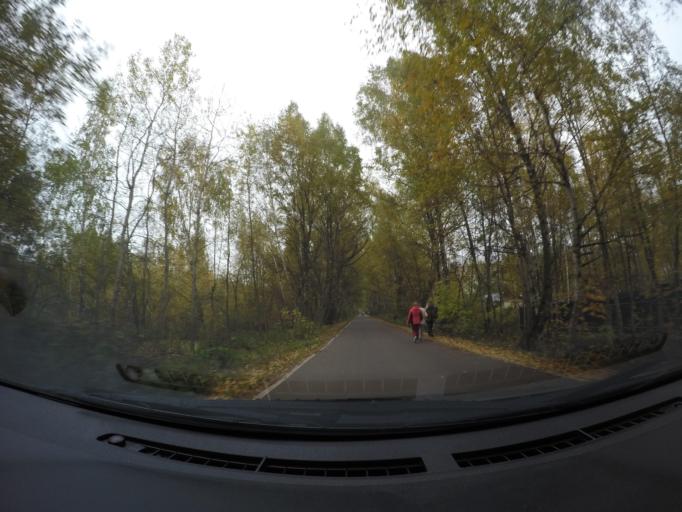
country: RU
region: Moskovskaya
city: Imeni Vorovskogo
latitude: 55.7299
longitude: 38.3199
